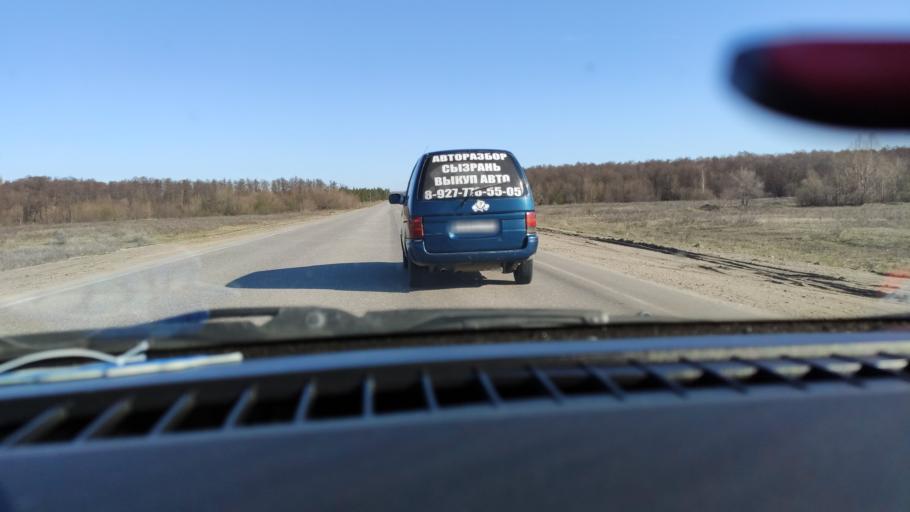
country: RU
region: Samara
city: Varlamovo
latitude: 53.1419
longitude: 48.2860
